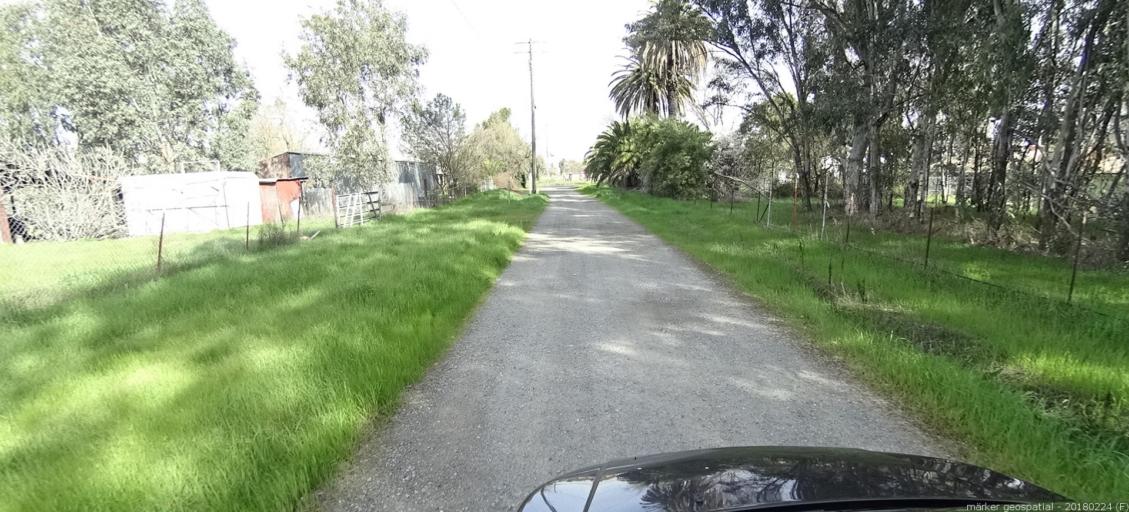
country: US
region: California
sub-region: Sacramento County
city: Rio Linda
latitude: 38.6832
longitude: -121.4708
